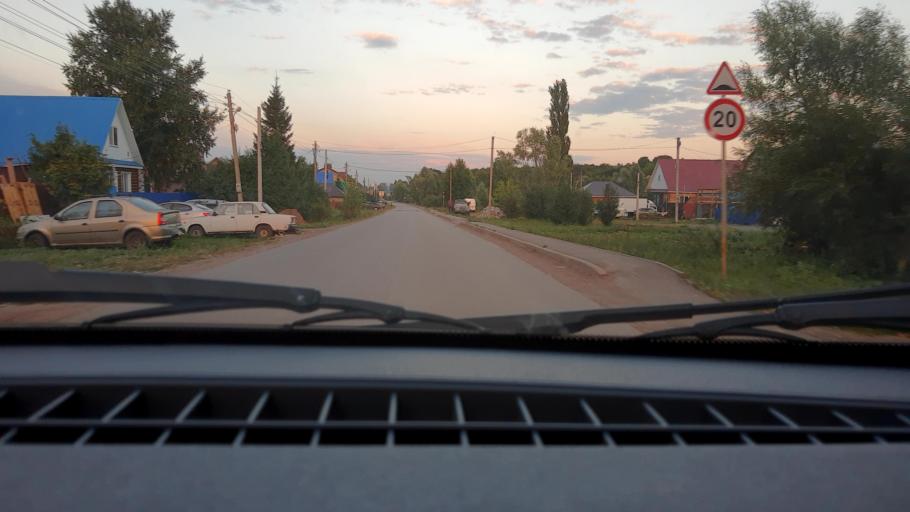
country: RU
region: Bashkortostan
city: Mikhaylovka
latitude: 54.7858
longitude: 55.8132
